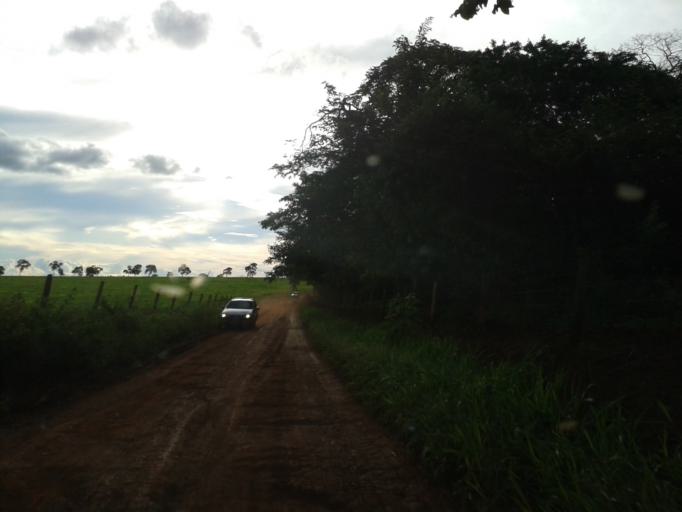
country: BR
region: Minas Gerais
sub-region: Capinopolis
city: Capinopolis
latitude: -18.7532
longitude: -49.8126
